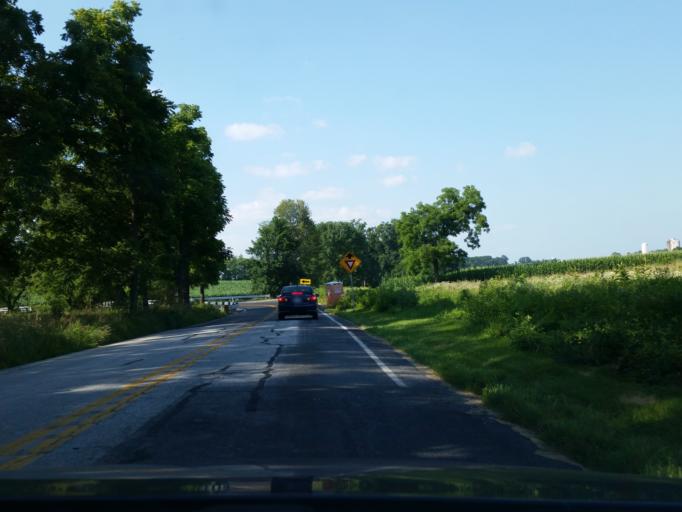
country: US
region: Pennsylvania
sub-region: Lancaster County
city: Mount Joy
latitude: 40.1694
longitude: -76.4971
